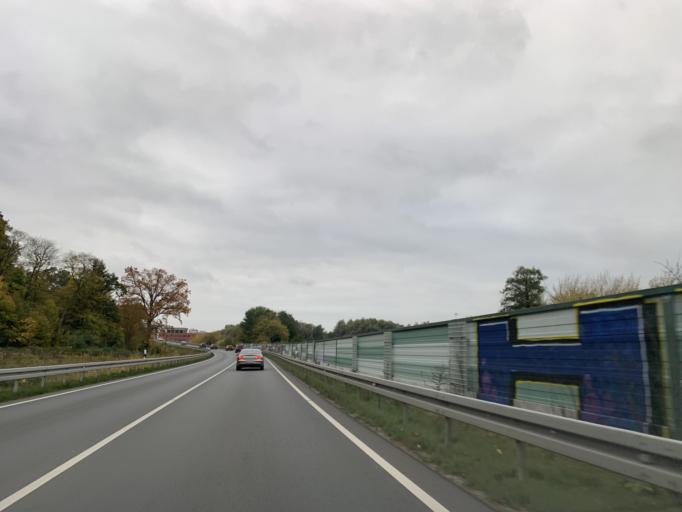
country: DE
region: Mecklenburg-Vorpommern
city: Neubrandenburg
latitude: 53.5535
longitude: 13.2780
